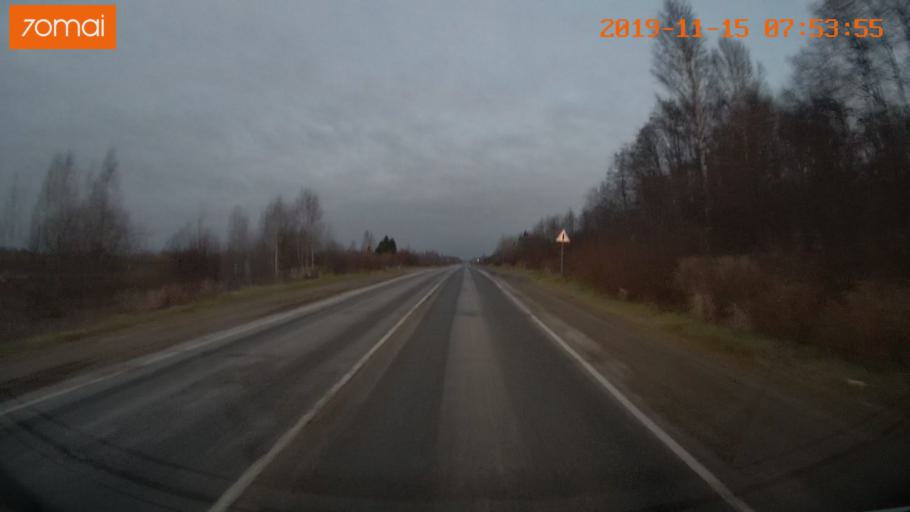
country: RU
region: Vologda
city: Cherepovets
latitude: 58.8938
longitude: 38.1815
